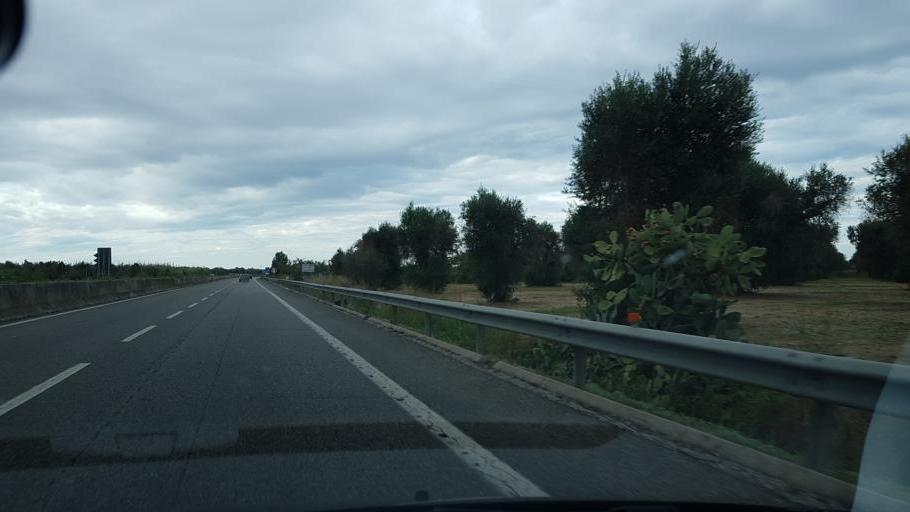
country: IT
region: Apulia
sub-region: Provincia di Brindisi
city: San Pietro Vernotico
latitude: 40.5212
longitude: 18.0166
